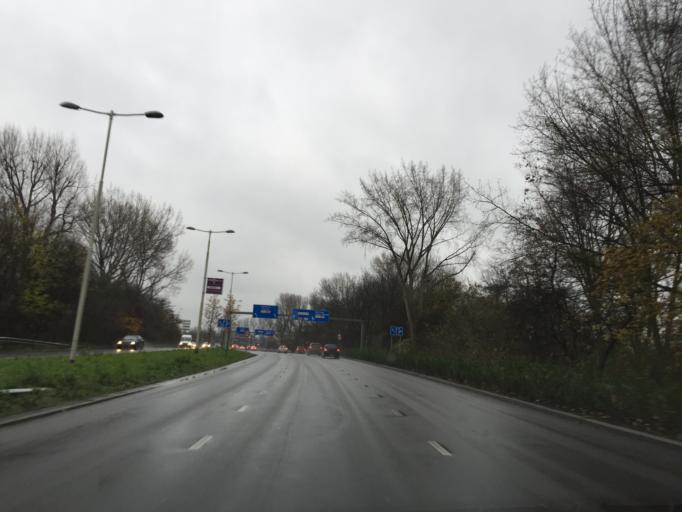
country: NL
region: South Holland
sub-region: Gemeente Rotterdam
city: Rotterdam
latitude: 51.9417
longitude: 4.4598
